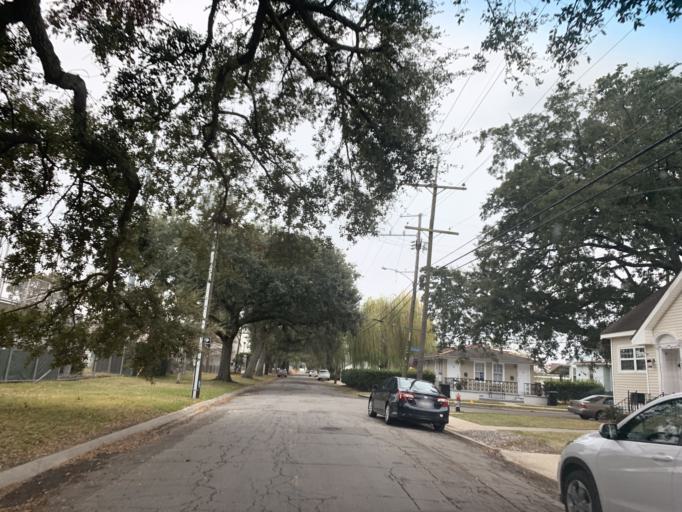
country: US
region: Louisiana
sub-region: Orleans Parish
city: New Orleans
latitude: 29.9873
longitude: -90.1072
